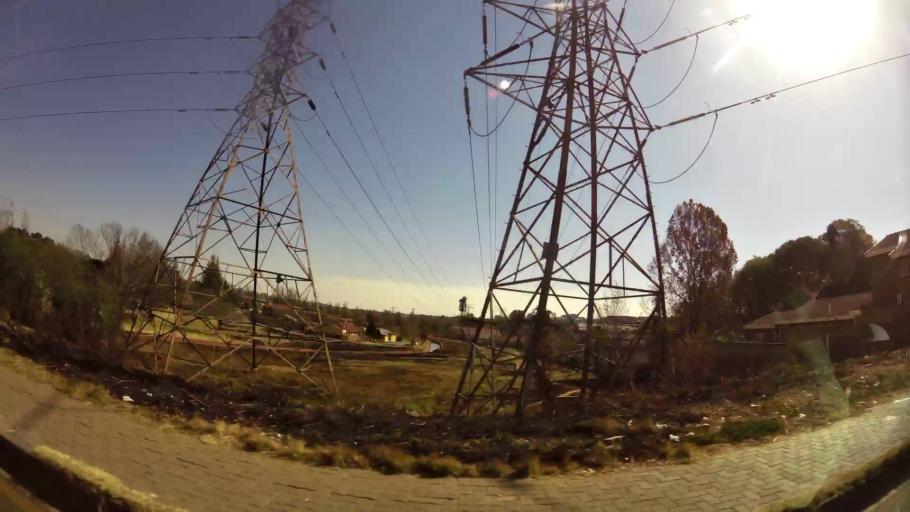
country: ZA
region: Gauteng
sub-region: City of Johannesburg Metropolitan Municipality
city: Johannesburg
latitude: -26.1923
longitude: 27.9644
